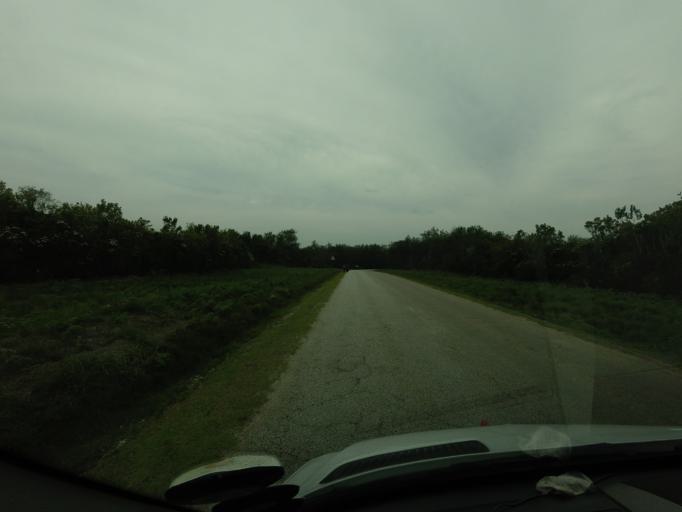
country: ZA
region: Eastern Cape
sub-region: Cacadu District Municipality
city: Kareedouw
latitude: -33.9688
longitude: 23.8876
